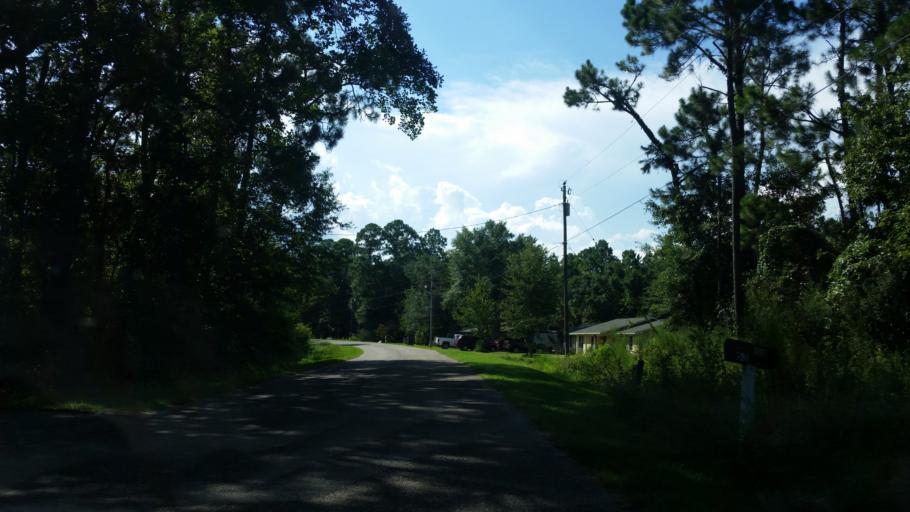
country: US
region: Florida
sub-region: Santa Rosa County
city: Pace
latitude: 30.5808
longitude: -87.1539
